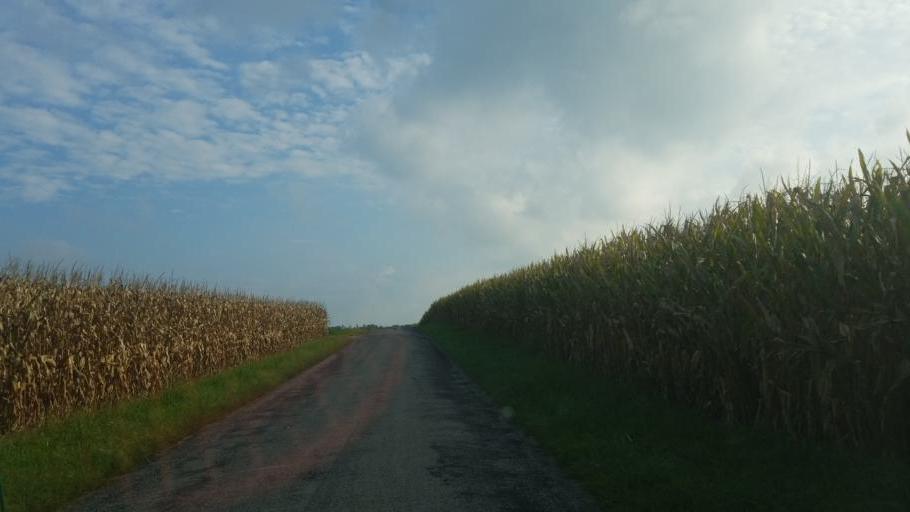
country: US
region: Ohio
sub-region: Wayne County
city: Wooster
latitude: 40.8476
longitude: -82.0337
